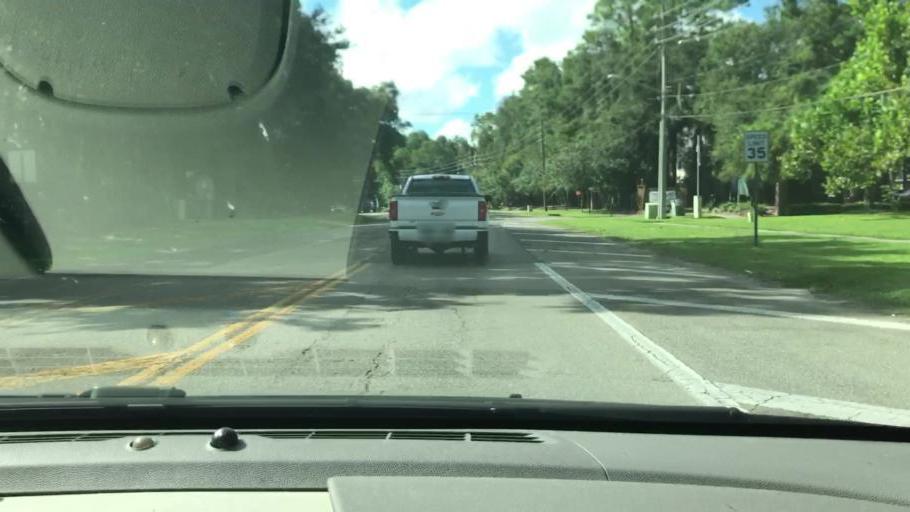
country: US
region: Florida
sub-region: Alachua County
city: Gainesville
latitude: 29.6527
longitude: -82.4089
